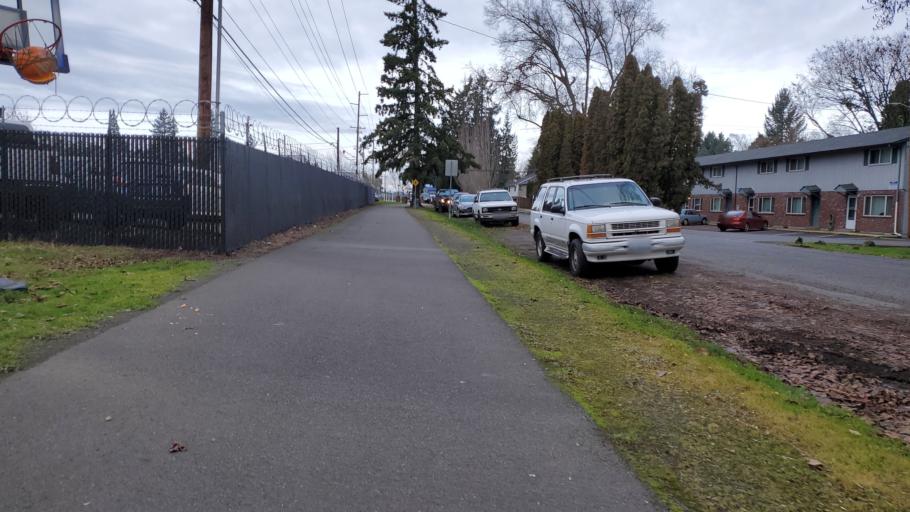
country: US
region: Oregon
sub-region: Clackamas County
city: Jennings Lodge
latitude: 45.3889
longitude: -122.6094
